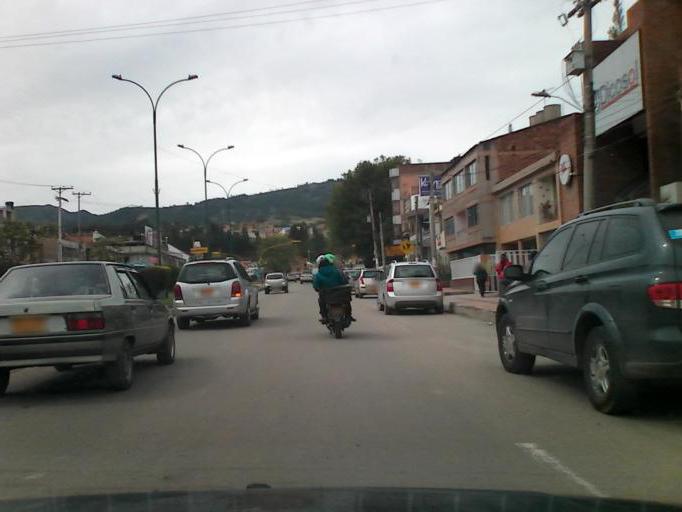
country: CO
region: Boyaca
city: Duitama
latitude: 5.8224
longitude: -73.0372
